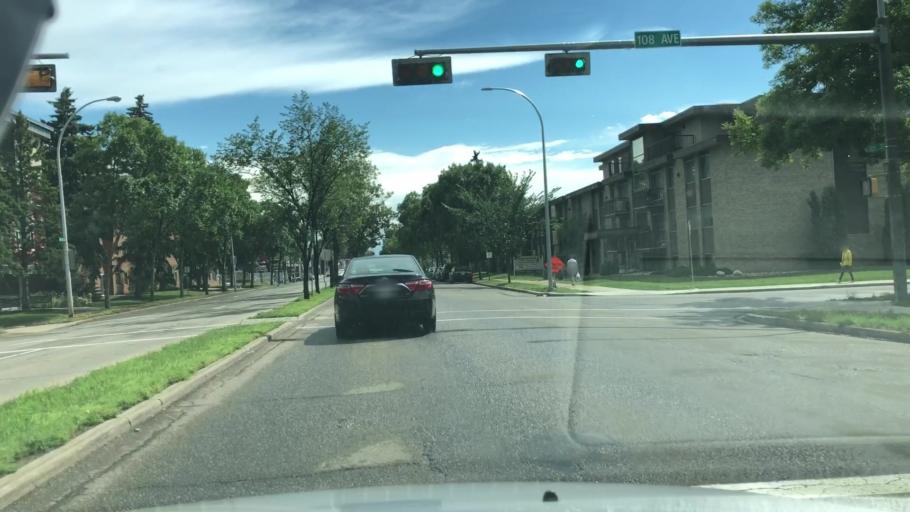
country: CA
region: Alberta
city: Edmonton
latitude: 53.5532
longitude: -113.5085
